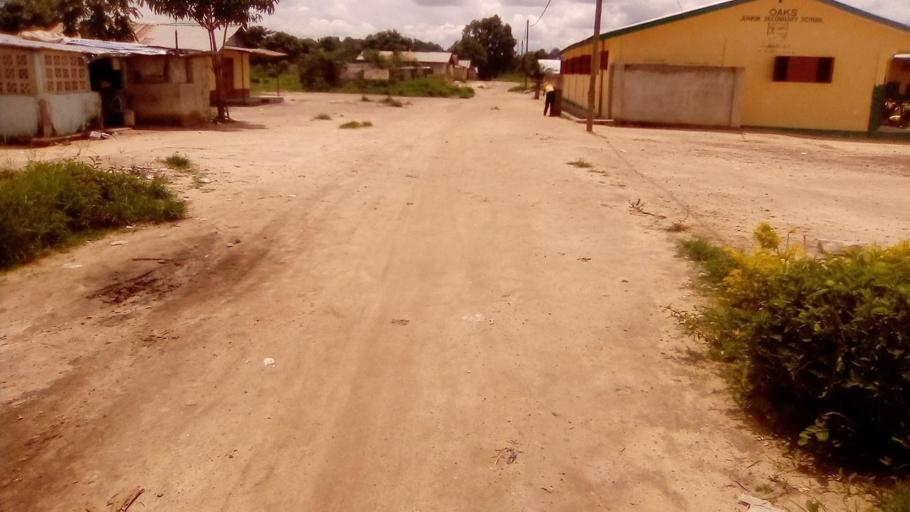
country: SL
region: Southern Province
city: Bo
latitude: 7.9368
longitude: -11.7477
